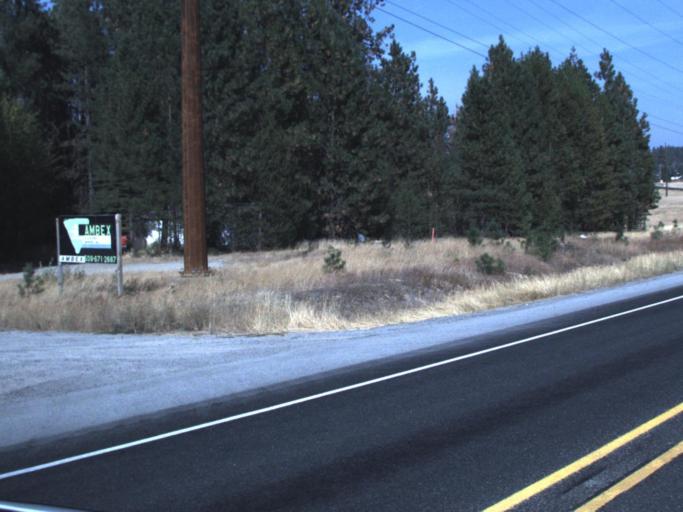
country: US
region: Washington
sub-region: Pend Oreille County
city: Newport
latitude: 48.0973
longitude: -117.2587
